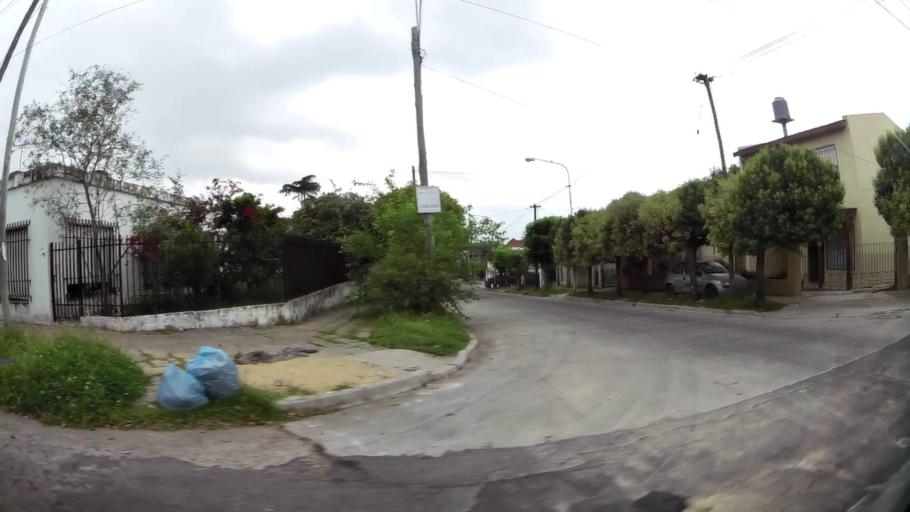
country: AR
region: Buenos Aires
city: San Justo
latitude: -34.7093
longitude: -58.5208
